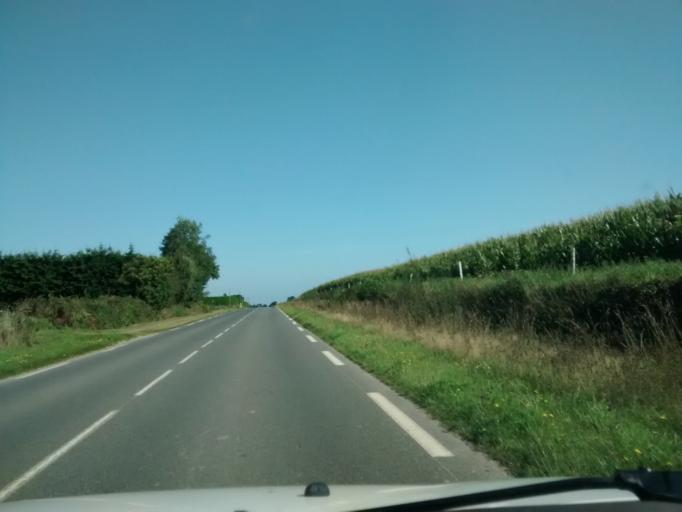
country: FR
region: Brittany
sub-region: Departement des Cotes-d'Armor
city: Tredarzec
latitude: 48.7966
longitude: -3.2011
